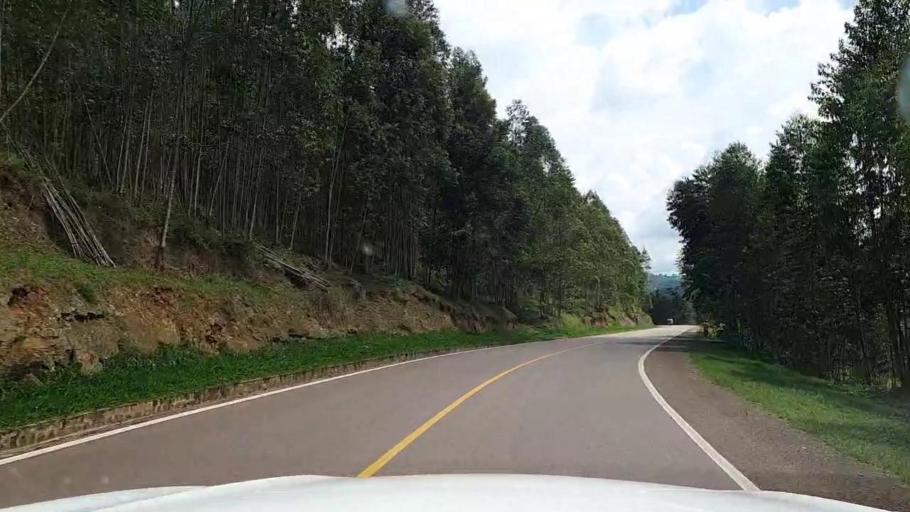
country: RW
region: Kigali
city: Kigali
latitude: -1.8210
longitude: 30.0844
